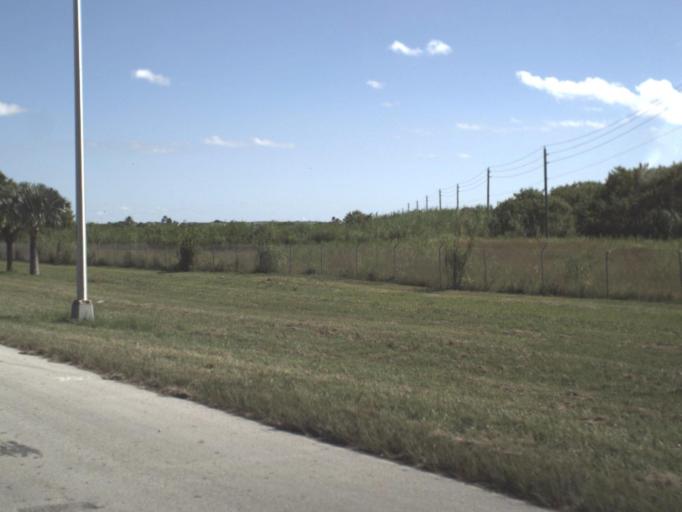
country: US
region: Florida
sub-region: Miami-Dade County
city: Florida City
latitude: 25.4555
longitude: -80.4721
